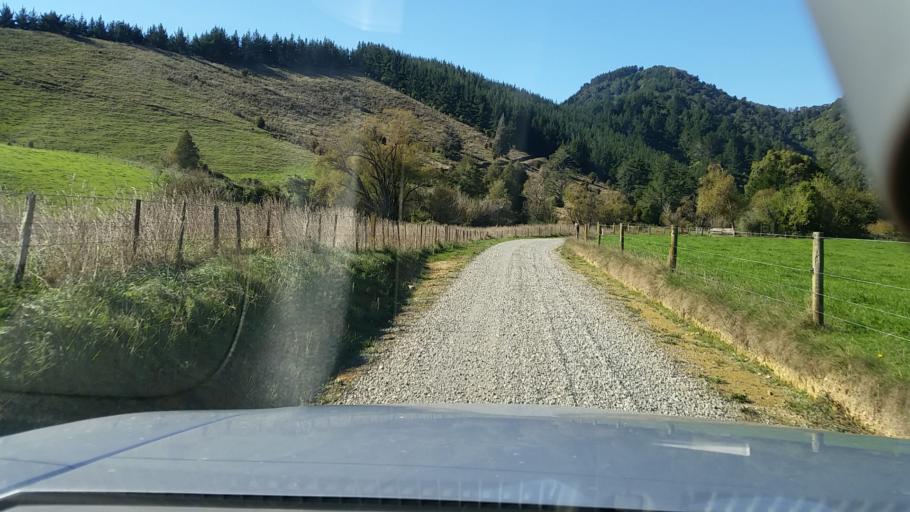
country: NZ
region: Nelson
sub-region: Nelson City
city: Nelson
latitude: -41.2214
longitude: 173.6103
